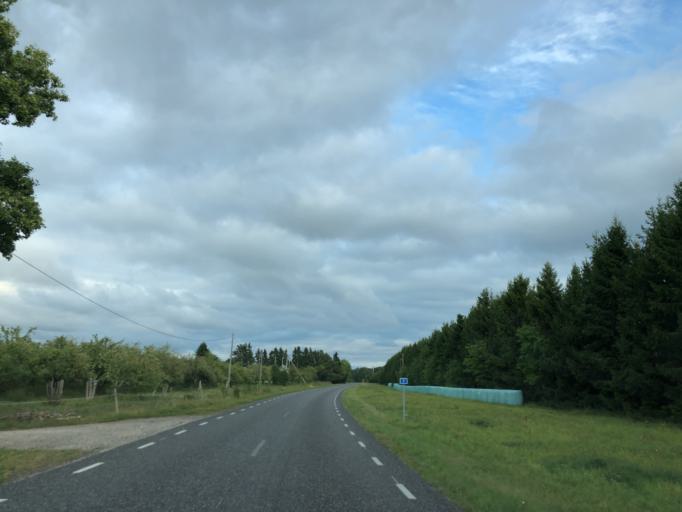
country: EE
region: Hiiumaa
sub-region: Kaerdla linn
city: Kardla
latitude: 58.7899
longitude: 22.8127
